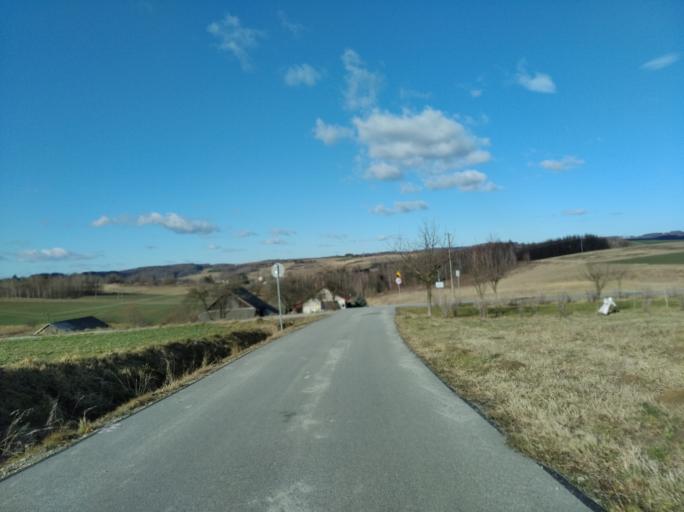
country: PL
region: Subcarpathian Voivodeship
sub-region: Powiat strzyzowski
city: Wisniowa
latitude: 49.9015
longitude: 21.6826
